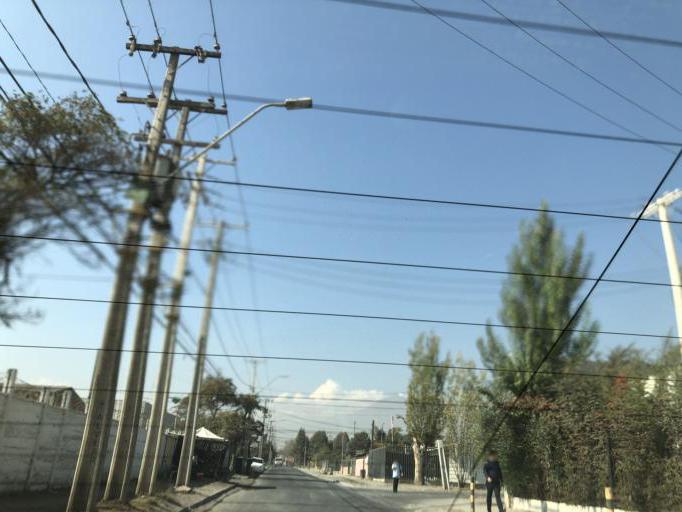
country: CL
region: Santiago Metropolitan
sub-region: Provincia de Cordillera
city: Puente Alto
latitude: -33.6195
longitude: -70.5708
